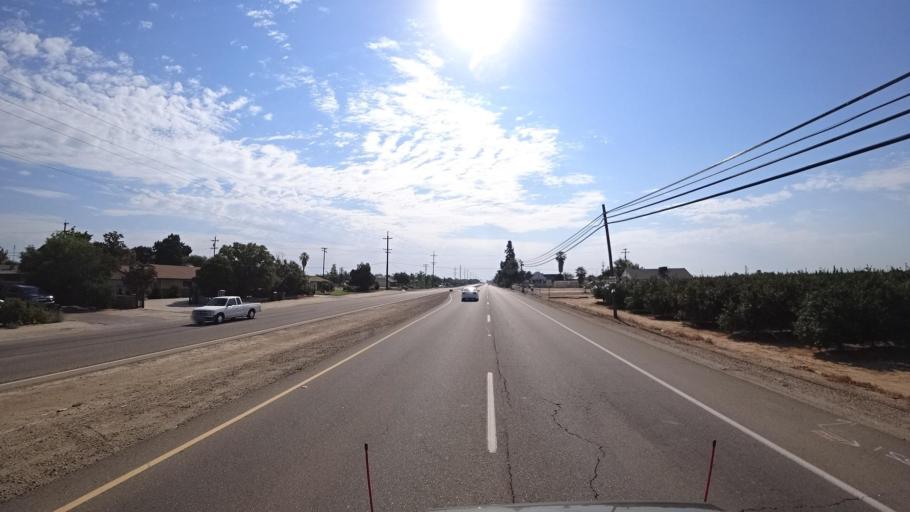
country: US
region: California
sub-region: Fresno County
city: Sunnyside
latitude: 36.7074
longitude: -119.6968
